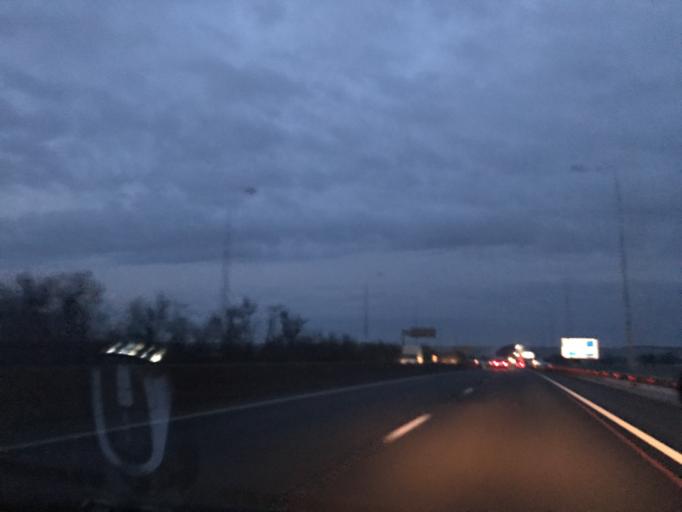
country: RU
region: Rostov
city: Samarskoye
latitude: 47.0085
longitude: 39.7324
